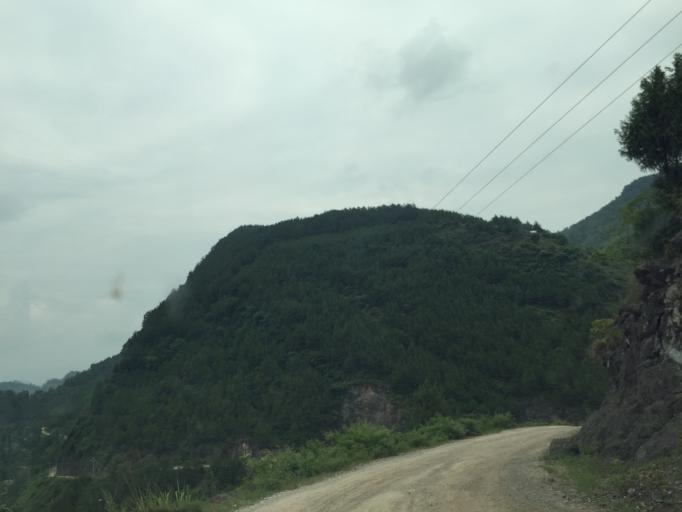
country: CN
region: Guizhou Sheng
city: Tongjing
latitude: 28.3728
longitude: 108.2419
